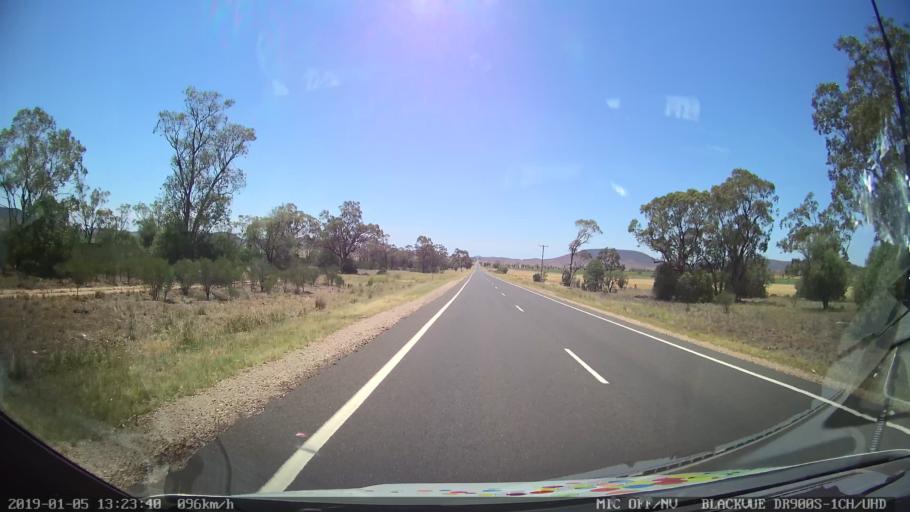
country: AU
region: New South Wales
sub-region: Gunnedah
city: Gunnedah
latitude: -31.0761
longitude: 149.9782
